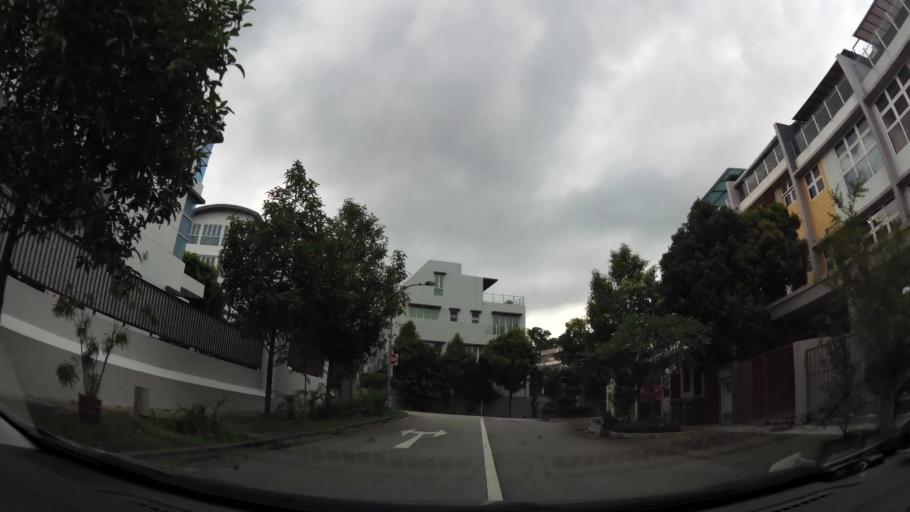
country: MY
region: Johor
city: Kampung Pasir Gudang Baru
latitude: 1.4598
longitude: 103.8384
